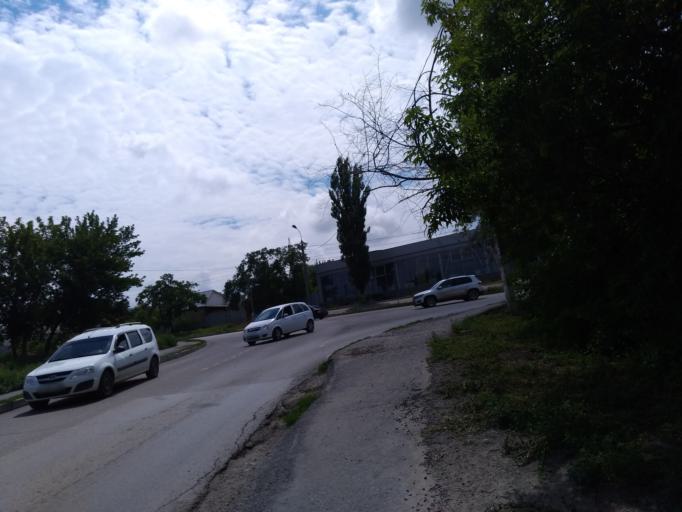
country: RU
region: Volgograd
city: Volgograd
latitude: 48.7107
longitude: 44.4652
